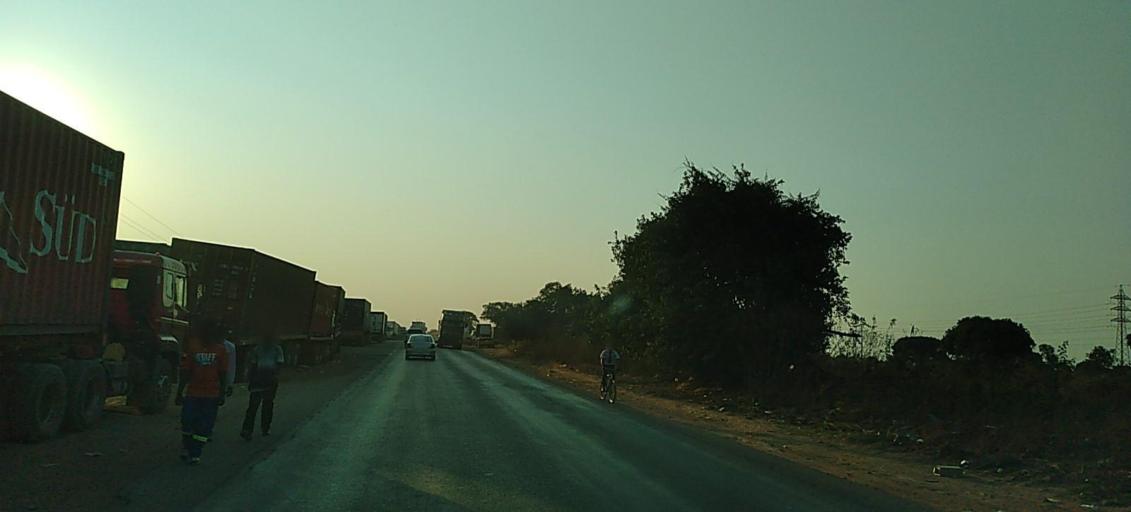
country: ZM
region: Copperbelt
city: Ndola
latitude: -13.0261
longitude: 28.6778
